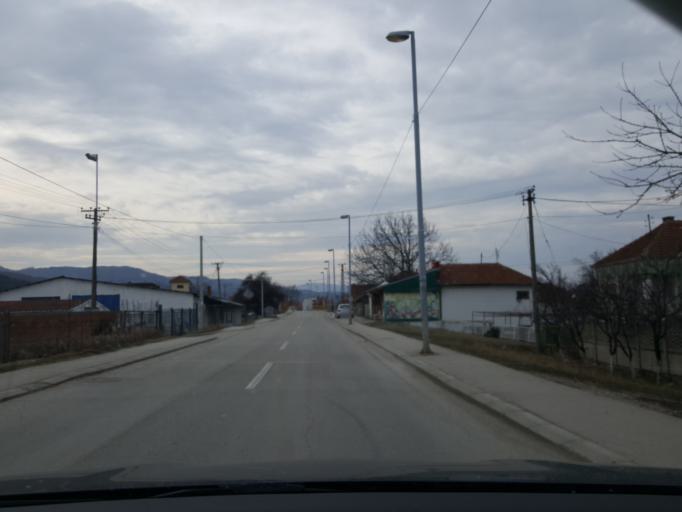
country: RS
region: Central Serbia
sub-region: Pirotski Okrug
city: Dimitrovgrad
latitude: 43.0110
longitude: 22.7552
